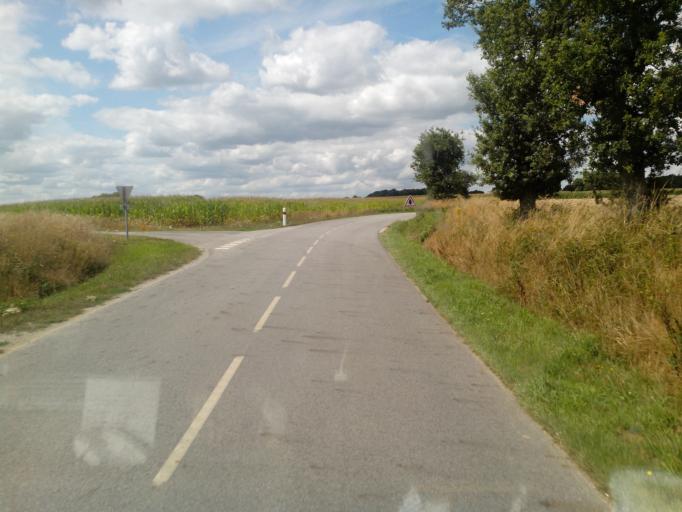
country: FR
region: Brittany
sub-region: Departement du Morbihan
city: Guilliers
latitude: 48.0487
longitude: -2.4101
